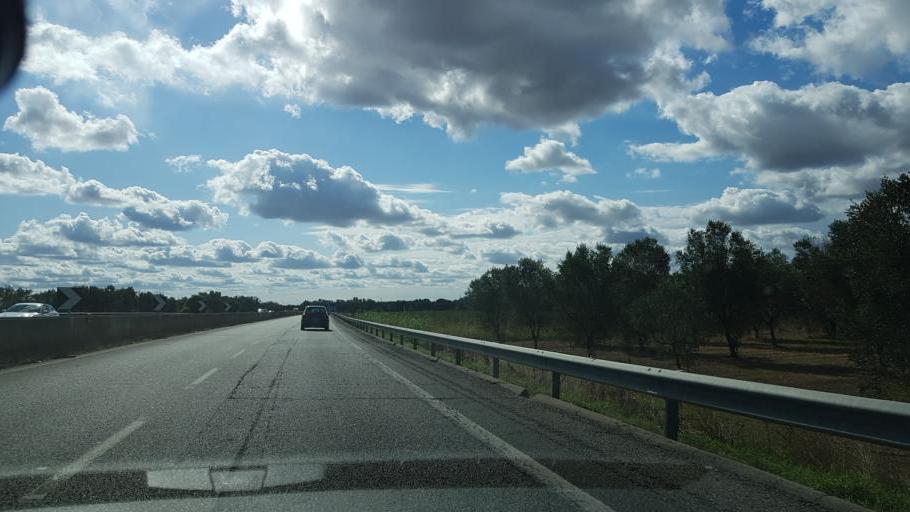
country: IT
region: Apulia
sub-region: Provincia di Brindisi
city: San Pietro Vernotico
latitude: 40.5323
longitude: 18.0095
